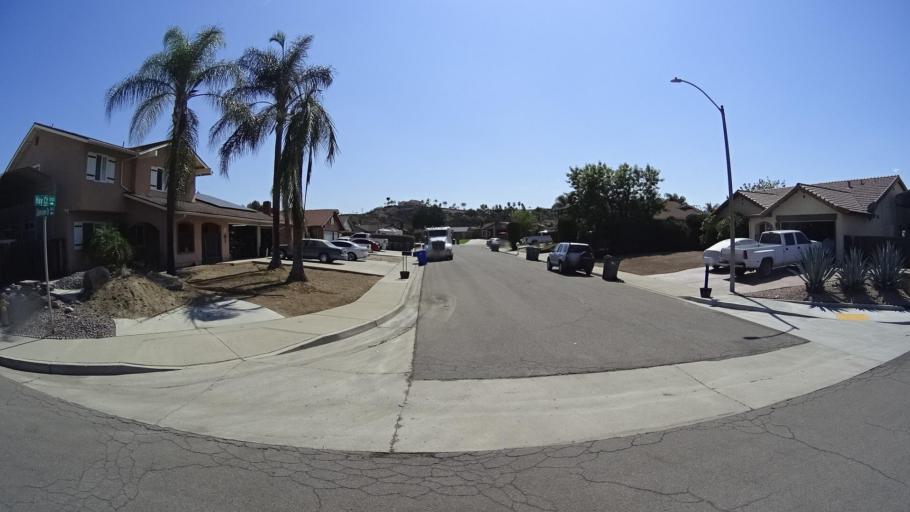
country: US
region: California
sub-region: San Diego County
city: Winter Gardens
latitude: 32.8296
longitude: -116.9201
